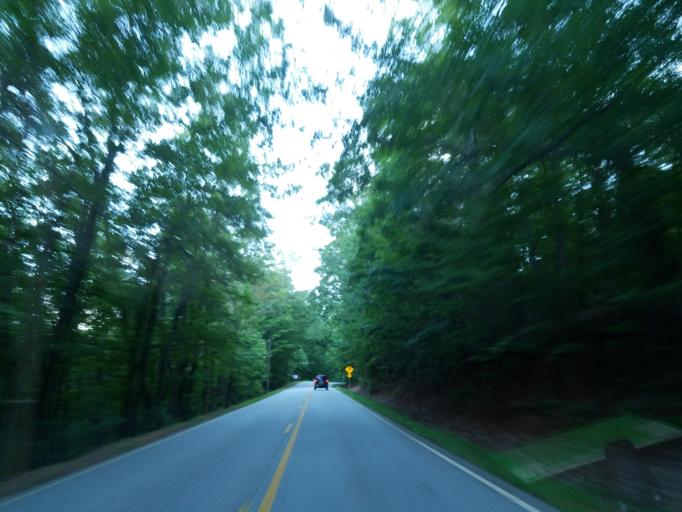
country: US
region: Georgia
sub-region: Lumpkin County
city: Dahlonega
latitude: 34.6195
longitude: -83.9599
